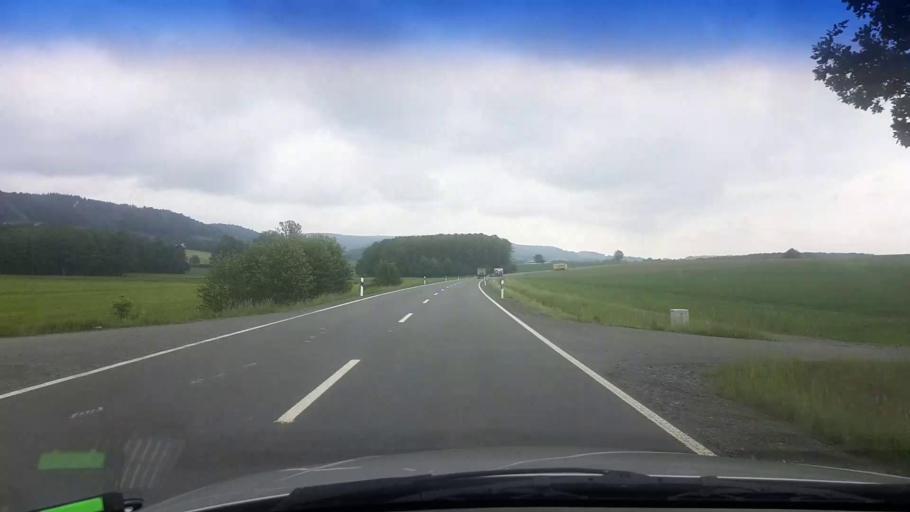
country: DE
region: Bavaria
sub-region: Upper Franconia
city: Gesees
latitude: 50.0255
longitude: 11.6606
